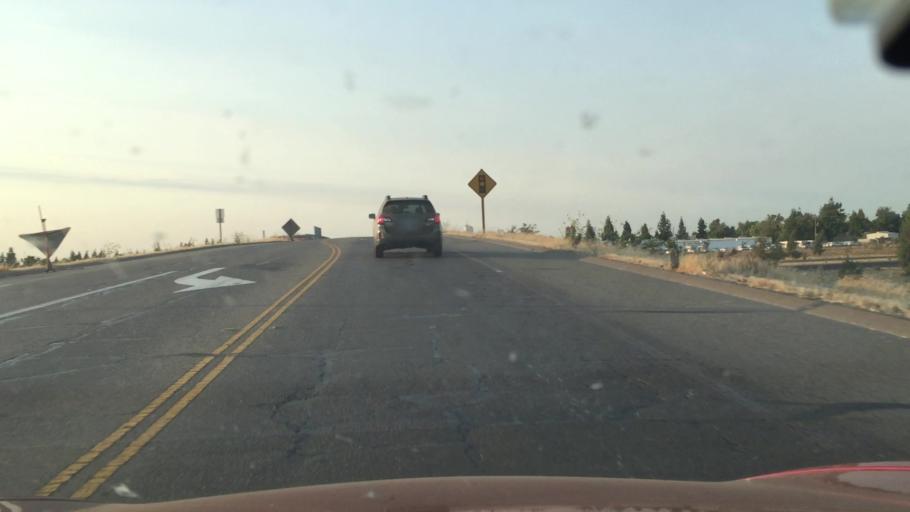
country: US
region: California
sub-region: San Joaquin County
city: Manteca
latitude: 37.7822
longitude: -121.2158
